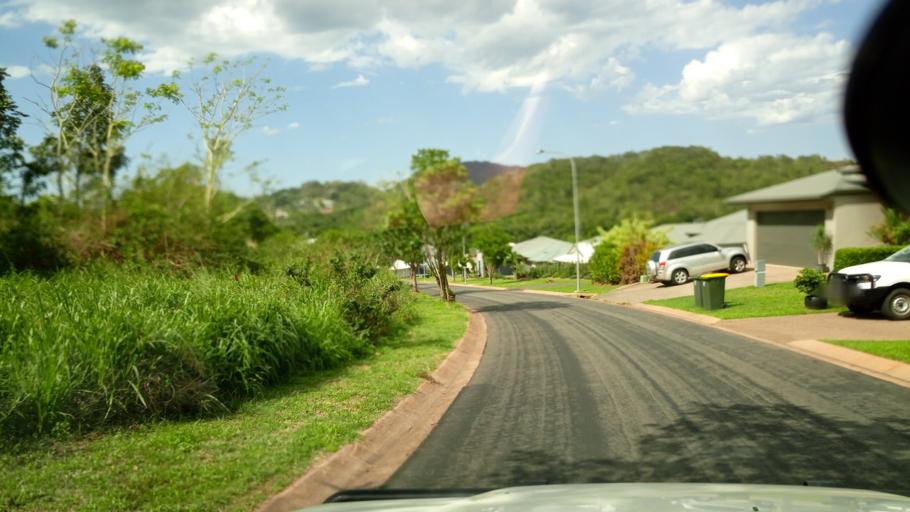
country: AU
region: Queensland
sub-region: Cairns
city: Woree
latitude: -16.9241
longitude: 145.7220
